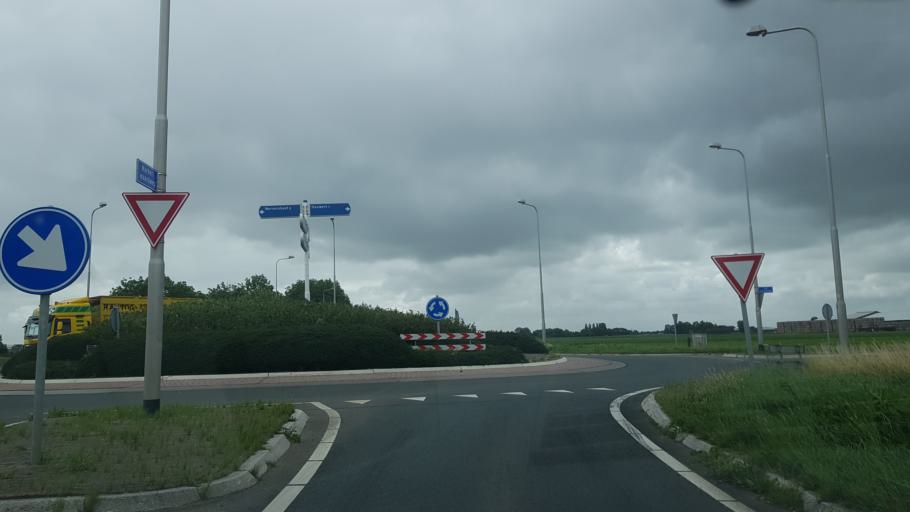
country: NL
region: North Holland
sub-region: Gemeente Medemblik
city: Medemblik
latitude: 52.7248
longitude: 5.1281
